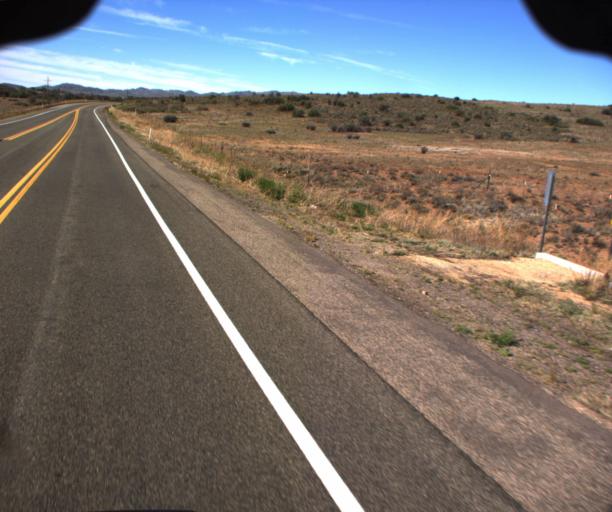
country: US
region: Arizona
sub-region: Yavapai County
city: Congress
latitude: 34.3131
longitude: -112.7085
